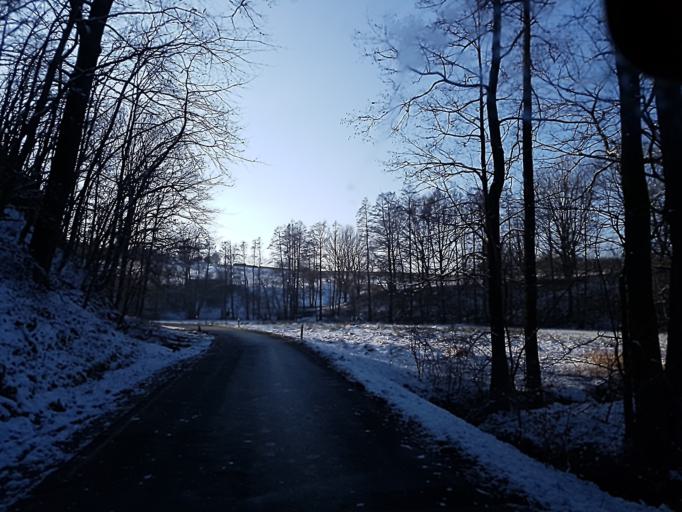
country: DE
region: Saxony
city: Hartha
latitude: 51.1429
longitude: 12.9810
